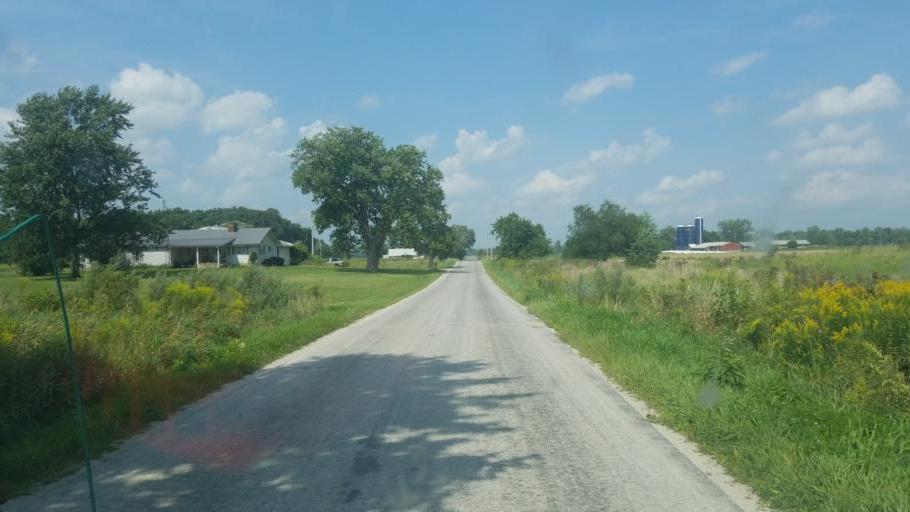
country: US
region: Ohio
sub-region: Huron County
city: Greenwich
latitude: 40.9610
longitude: -82.4316
